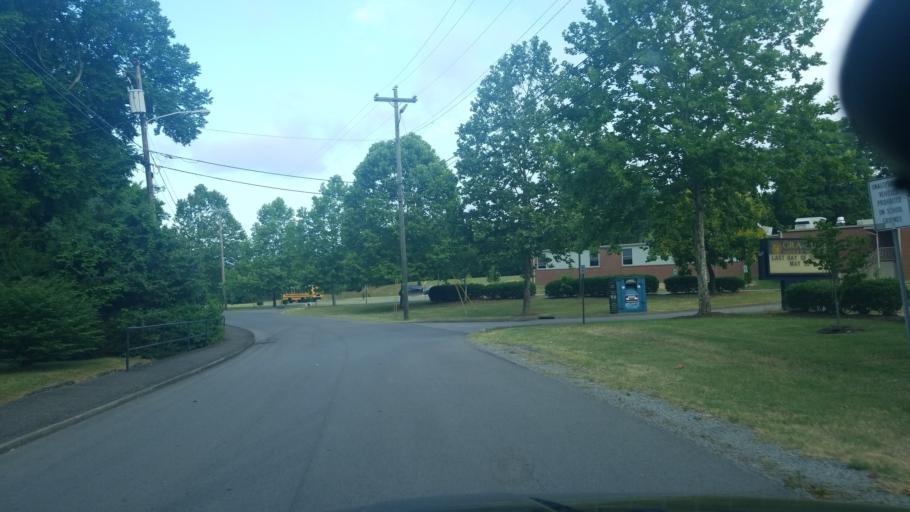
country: US
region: Tennessee
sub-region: Davidson County
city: Nashville
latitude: 36.2324
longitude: -86.7451
